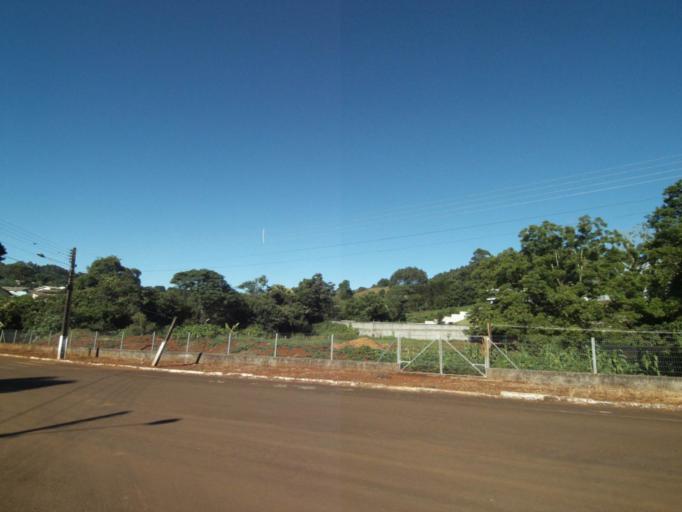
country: BR
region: Santa Catarina
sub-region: Sao Lourenco Do Oeste
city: Sao Lourenco dOeste
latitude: -26.2640
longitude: -52.7831
